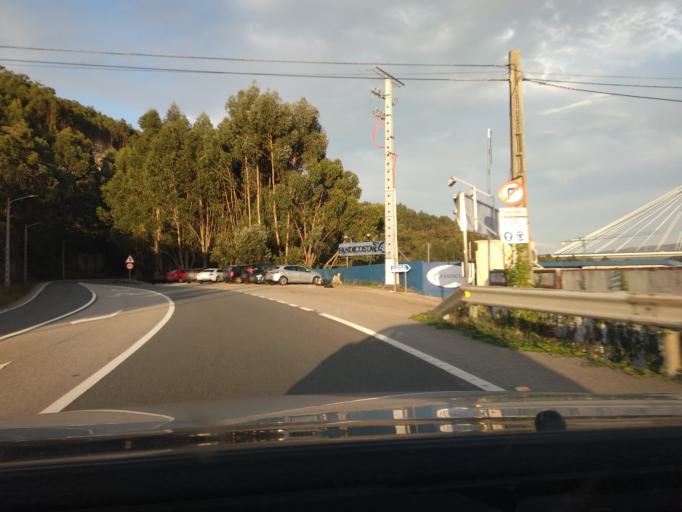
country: ES
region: Galicia
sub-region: Provincia de Pontevedra
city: Redondela
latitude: 42.2915
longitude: -8.6682
